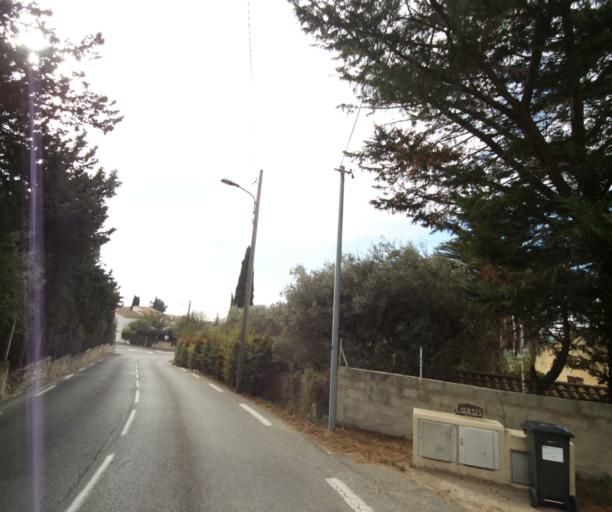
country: FR
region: Provence-Alpes-Cote d'Azur
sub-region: Departement des Bouches-du-Rhone
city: Ceyreste
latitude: 43.2193
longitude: 5.6401
